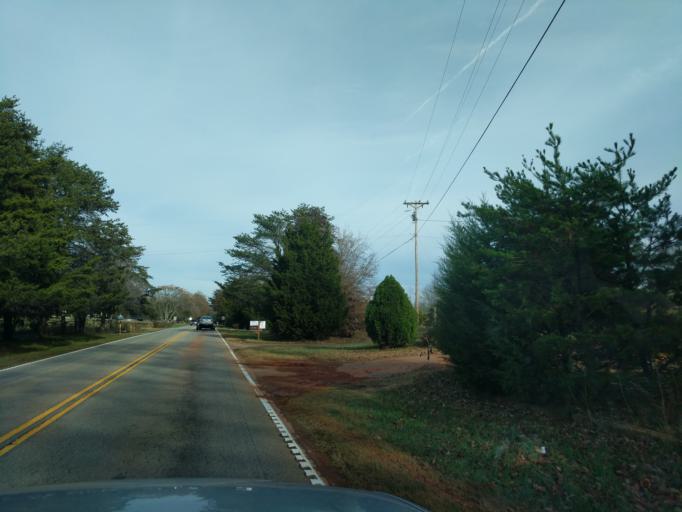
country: US
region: South Carolina
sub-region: Pickens County
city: Liberty
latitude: 34.7058
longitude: -82.6229
